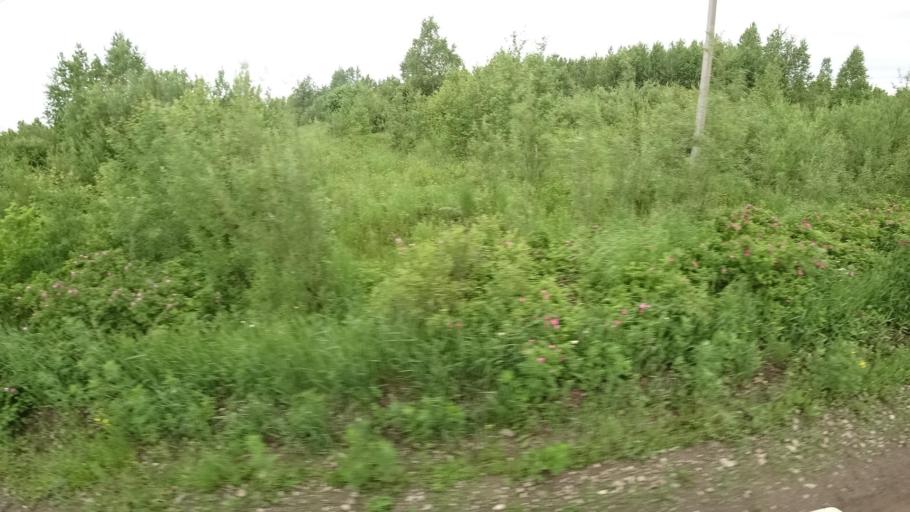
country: RU
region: Khabarovsk Krai
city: Amursk
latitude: 49.9148
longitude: 136.1604
